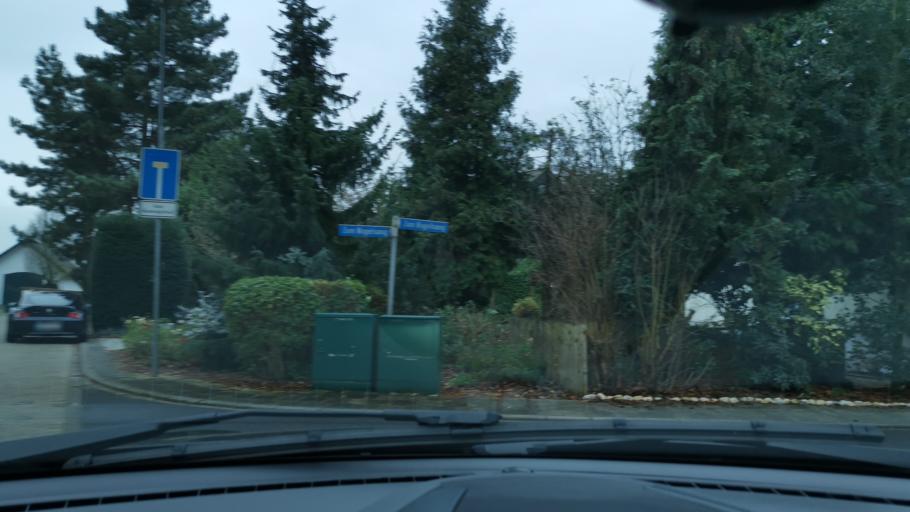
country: DE
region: North Rhine-Westphalia
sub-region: Regierungsbezirk Dusseldorf
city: Neubrueck
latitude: 51.1292
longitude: 6.6444
